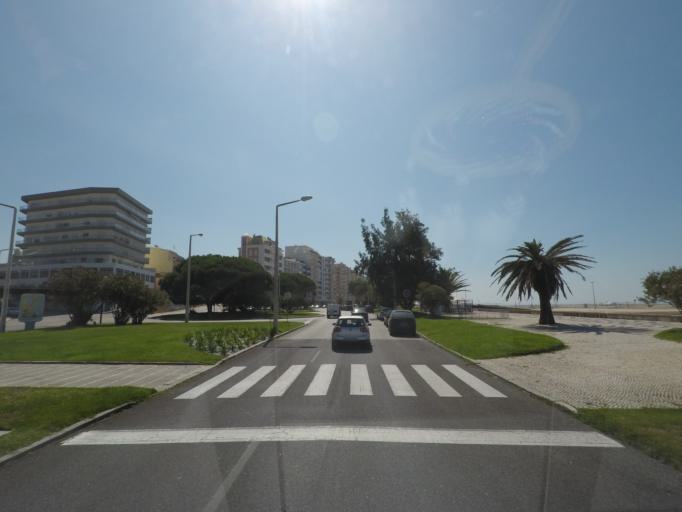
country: PT
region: Coimbra
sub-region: Figueira da Foz
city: Figueira da Foz
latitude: 40.1558
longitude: -8.8678
